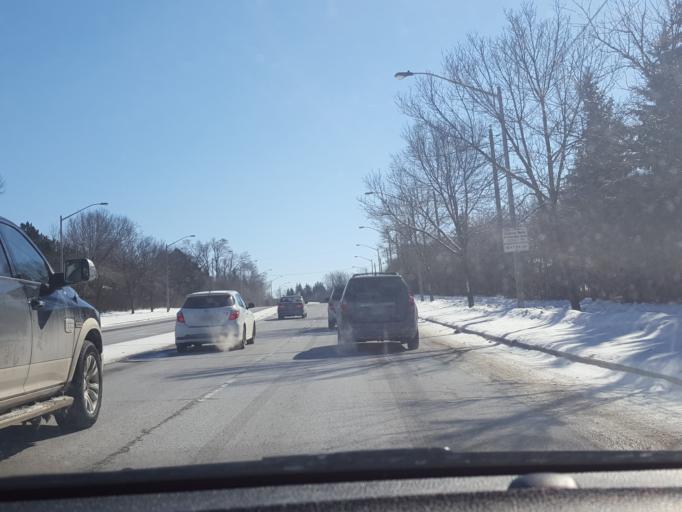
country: CA
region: Ontario
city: Waterloo
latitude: 43.4482
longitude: -80.5499
